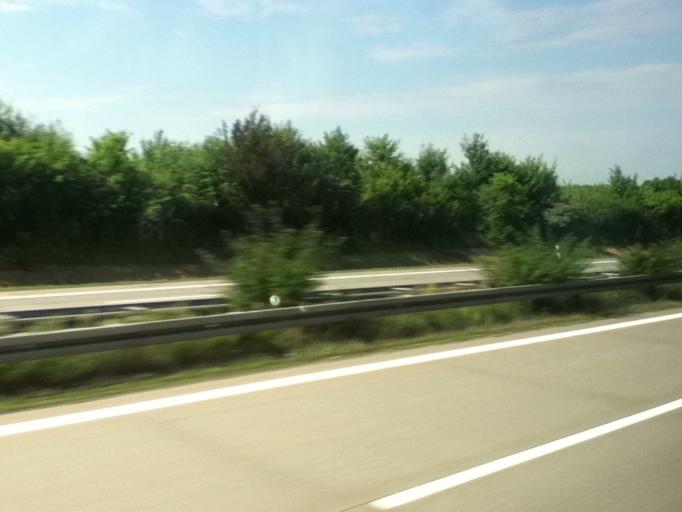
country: DE
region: Saxony
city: Crimmitschau
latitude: 50.8340
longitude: 12.4009
